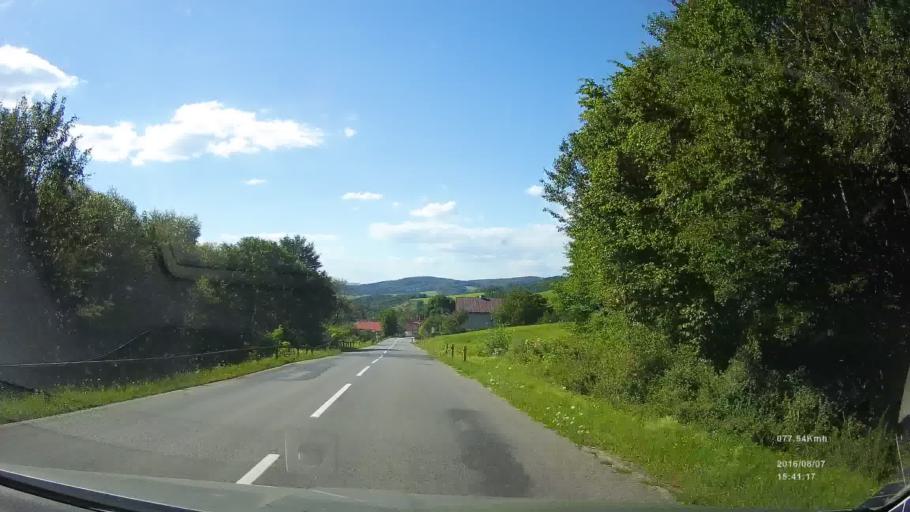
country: SK
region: Presovsky
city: Giraltovce
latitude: 49.1238
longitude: 21.5799
